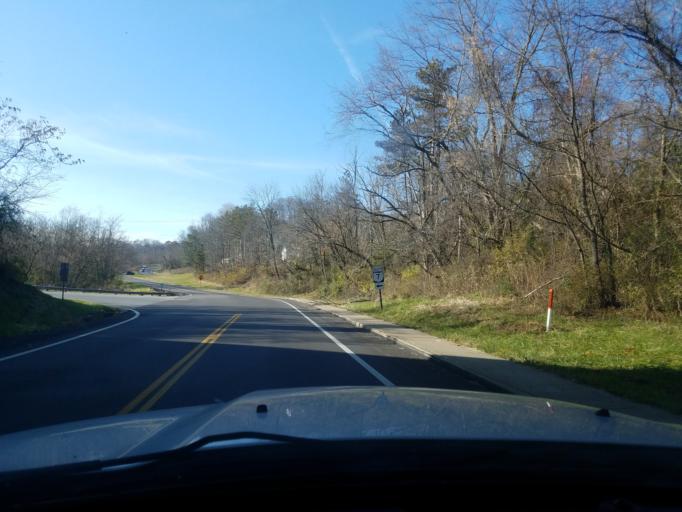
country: US
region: Ohio
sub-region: Washington County
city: Marietta
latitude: 39.4045
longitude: -81.4707
